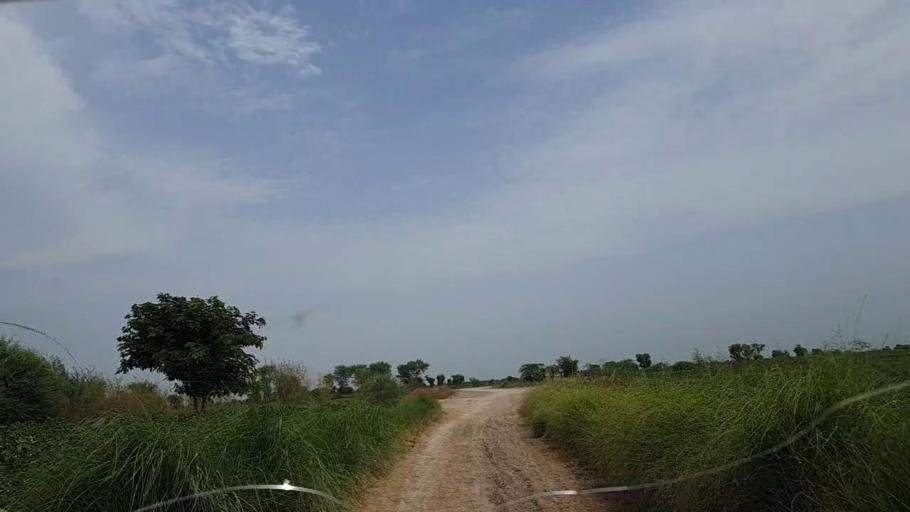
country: PK
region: Sindh
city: Naushahro Firoz
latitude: 26.8886
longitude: 68.0770
